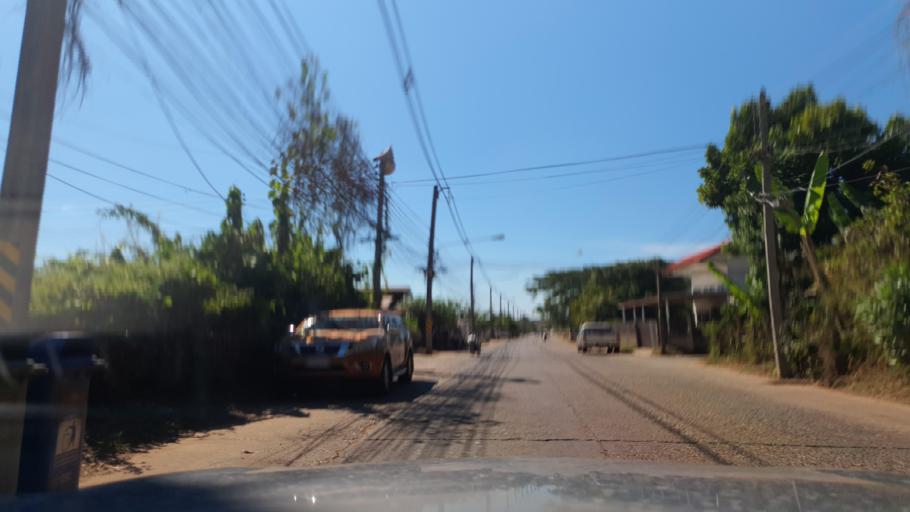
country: TH
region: Sakon Nakhon
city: Sakon Nakhon
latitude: 17.1632
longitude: 104.1231
